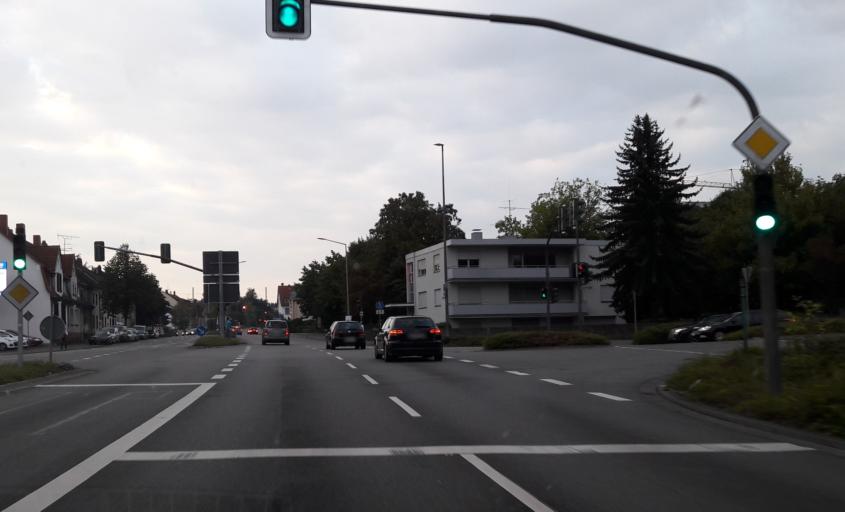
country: DE
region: Saarland
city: Homburg
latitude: 49.3192
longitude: 7.3345
